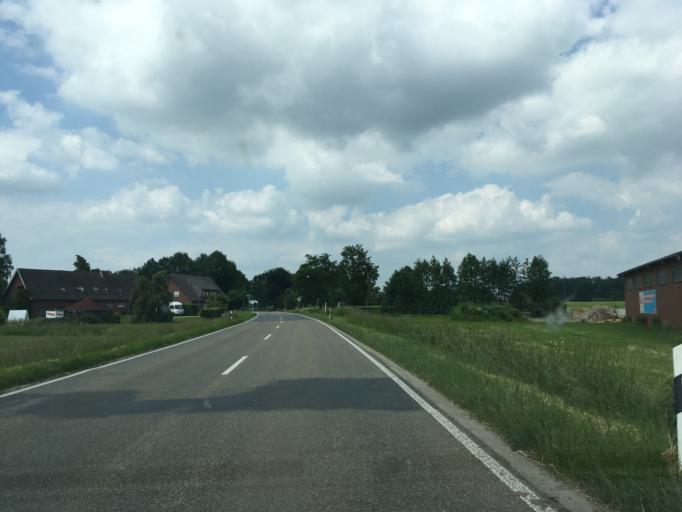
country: DE
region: North Rhine-Westphalia
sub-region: Regierungsbezirk Munster
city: Raesfeld
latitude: 51.7684
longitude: 6.8168
